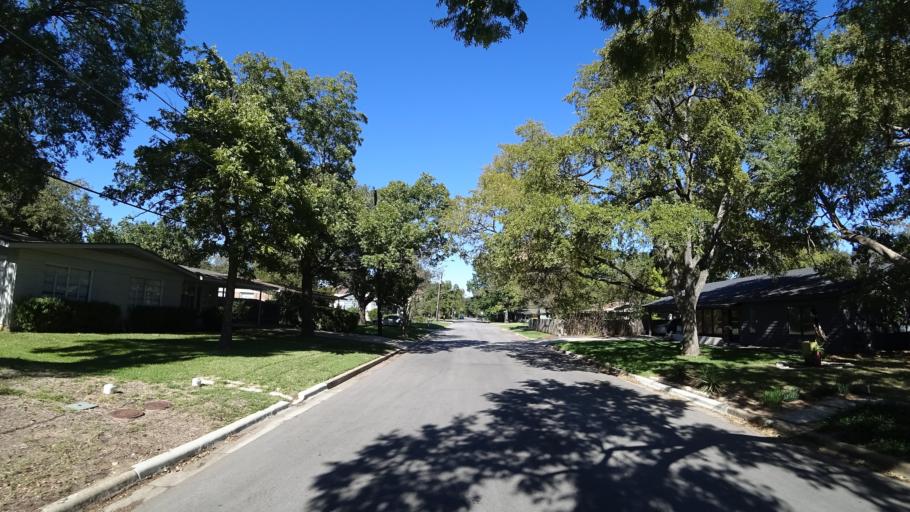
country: US
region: Texas
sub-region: Travis County
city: Austin
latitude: 30.3256
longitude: -97.7487
